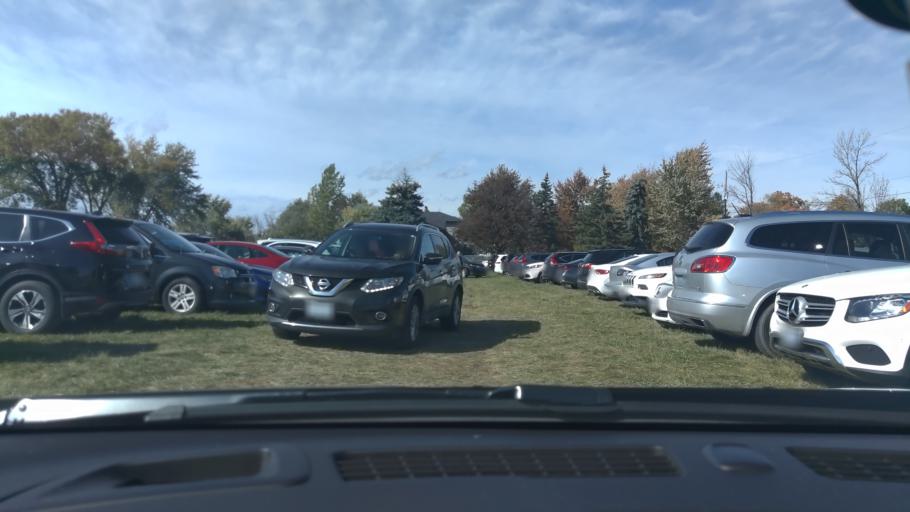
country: CA
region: Ontario
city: Brampton
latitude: 43.7867
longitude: -79.8499
